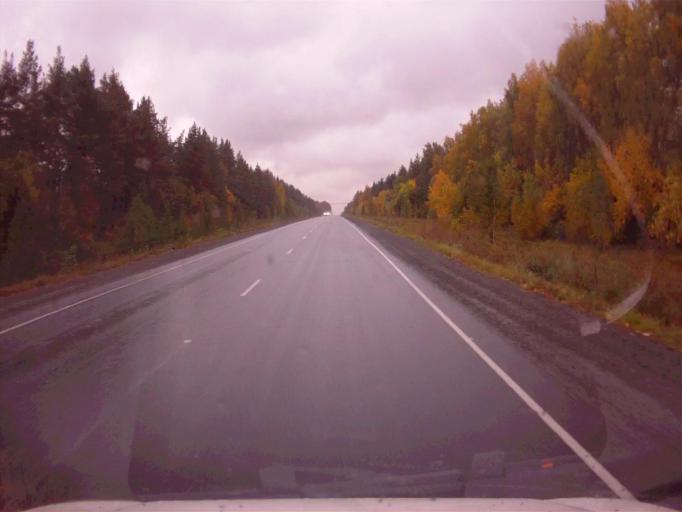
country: RU
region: Chelyabinsk
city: Roshchino
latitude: 55.3778
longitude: 61.1467
